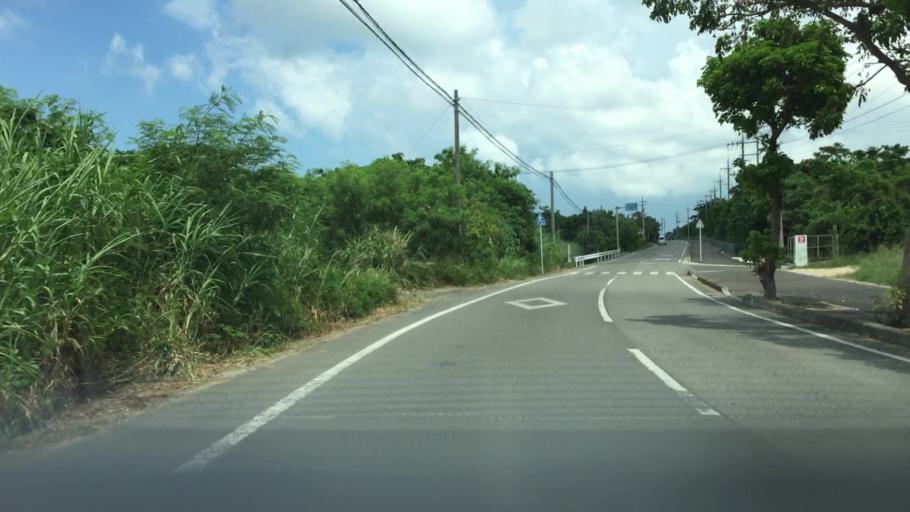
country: JP
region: Okinawa
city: Ishigaki
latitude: 24.3652
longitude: 124.1397
